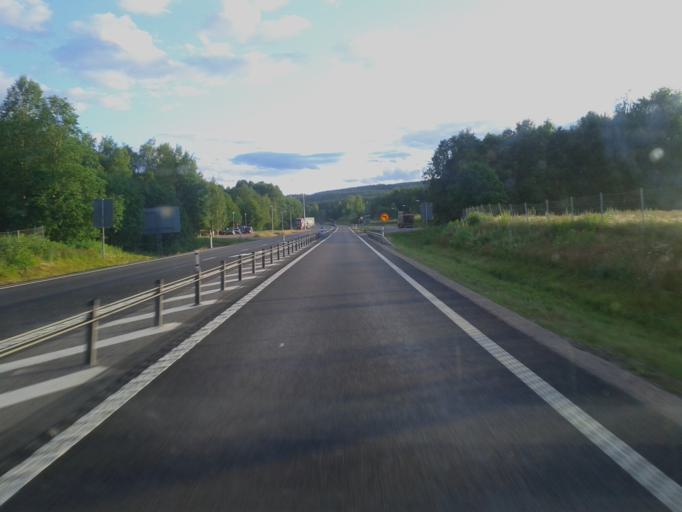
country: SE
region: Dalarna
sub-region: Borlange Kommun
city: Borlaenge
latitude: 60.4638
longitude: 15.3889
